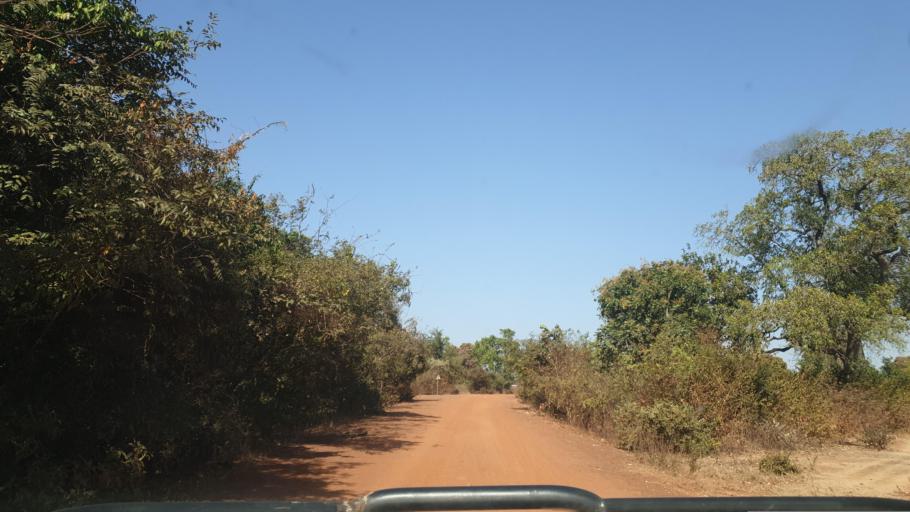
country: ML
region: Sikasso
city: Bougouni
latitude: 11.8107
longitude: -6.9328
